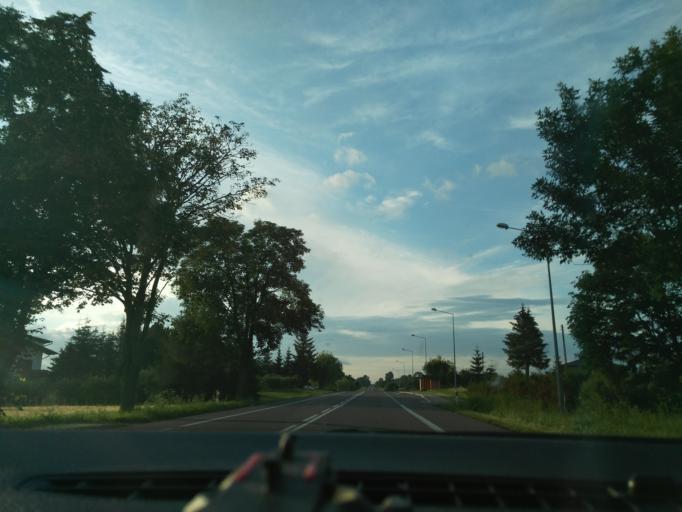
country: PL
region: Lublin Voivodeship
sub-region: Powiat lubelski
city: Niedrzwica Duza
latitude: 51.0638
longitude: 22.3814
